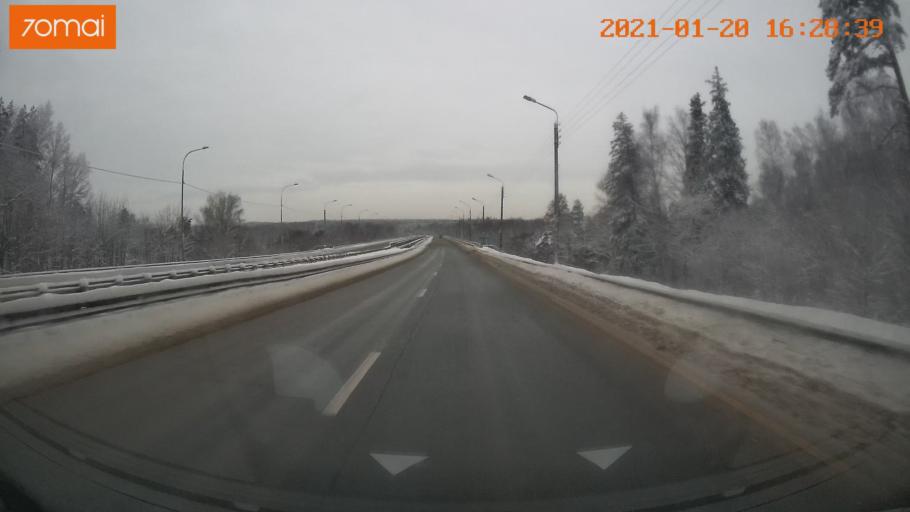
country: RU
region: Vladimir
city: Kameshkovo
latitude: 56.1959
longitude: 40.9124
